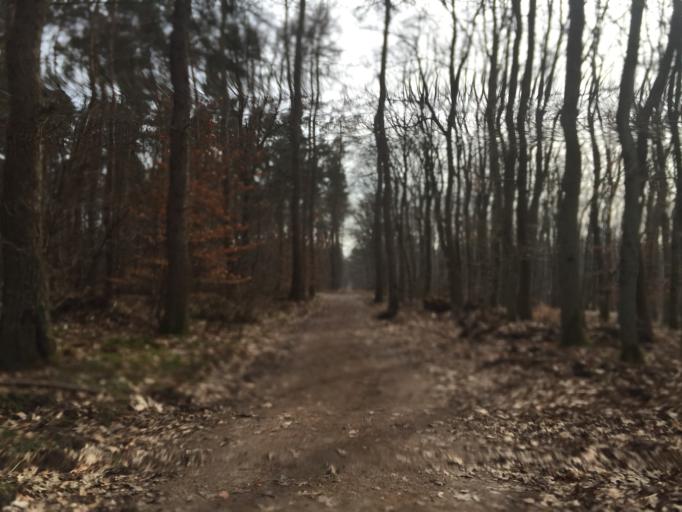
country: DE
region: Hesse
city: Viernheim
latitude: 49.5804
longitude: 8.5766
